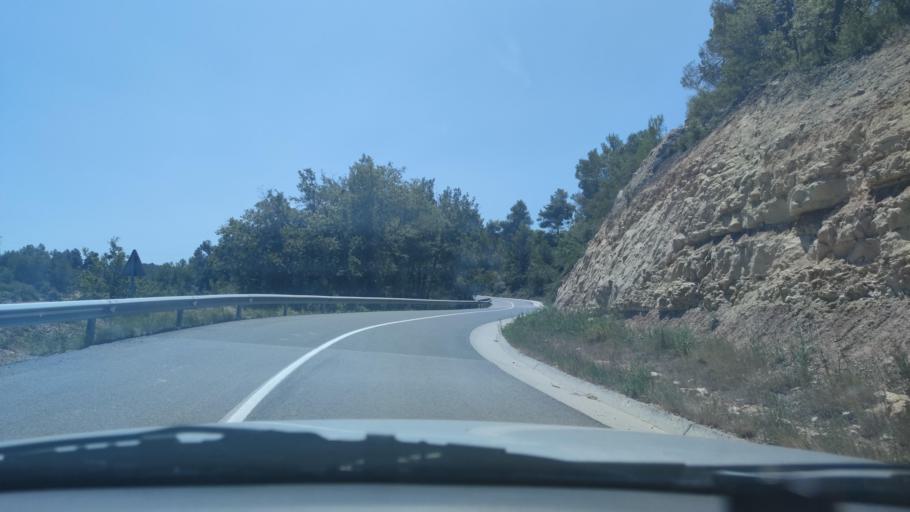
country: ES
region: Catalonia
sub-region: Provincia de Lleida
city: Vinaixa
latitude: 41.4126
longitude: 0.9564
